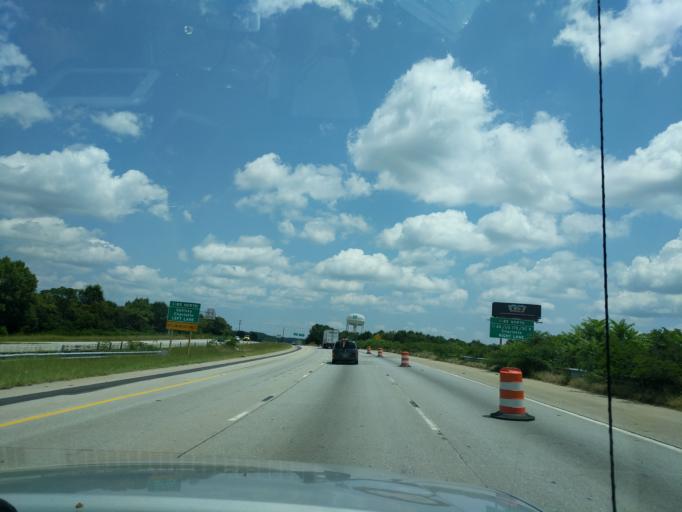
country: US
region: South Carolina
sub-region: Spartanburg County
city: Fairforest
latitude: 34.9650
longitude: -82.0317
